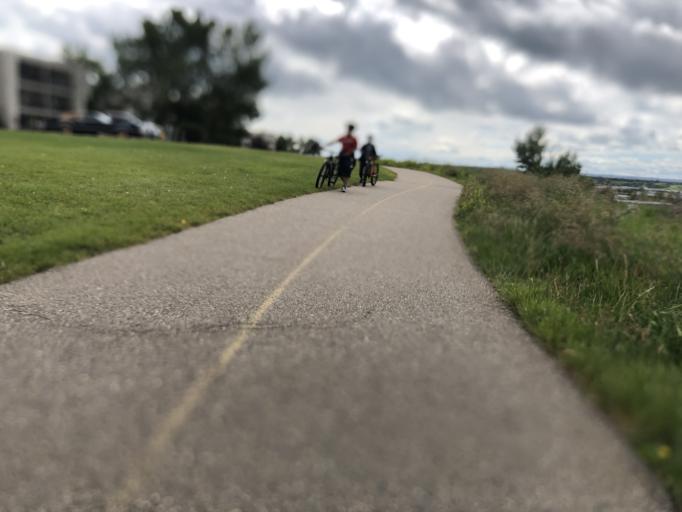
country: CA
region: Alberta
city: Calgary
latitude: 50.9971
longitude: -114.0230
